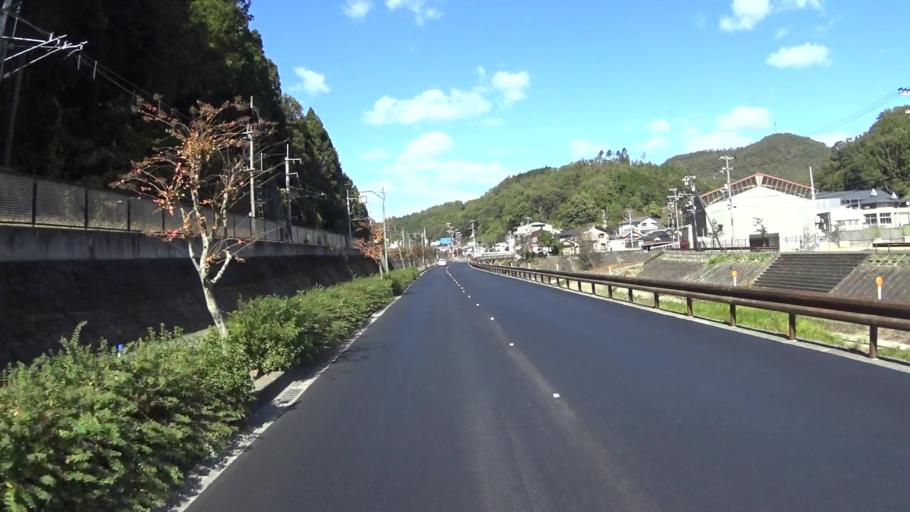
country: JP
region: Kyoto
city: Kameoka
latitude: 35.1592
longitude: 135.5056
